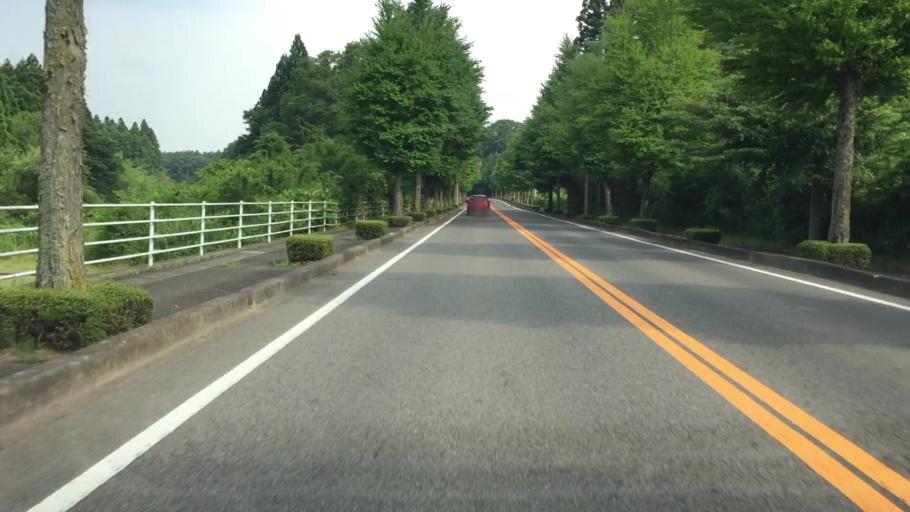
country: JP
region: Tochigi
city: Kuroiso
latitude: 36.9821
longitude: 139.9610
